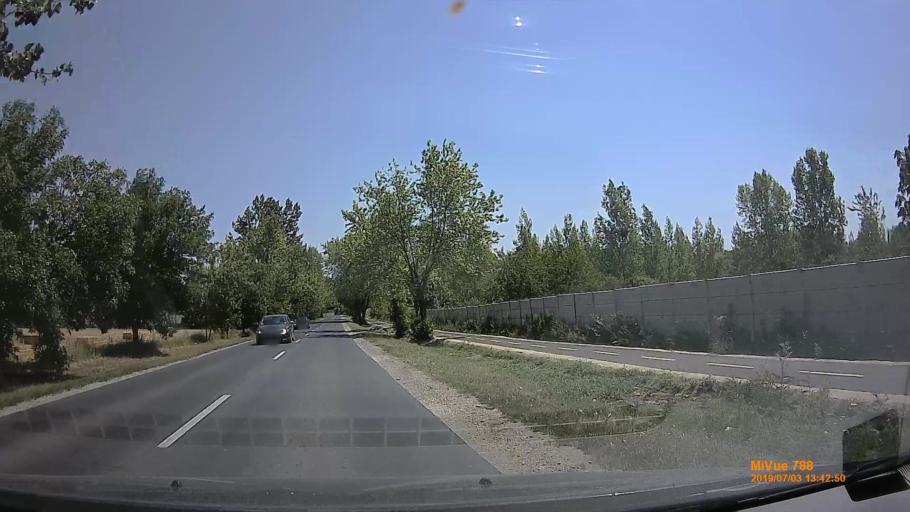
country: HU
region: Gyor-Moson-Sopron
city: Gyor
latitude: 47.7160
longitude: 17.6188
